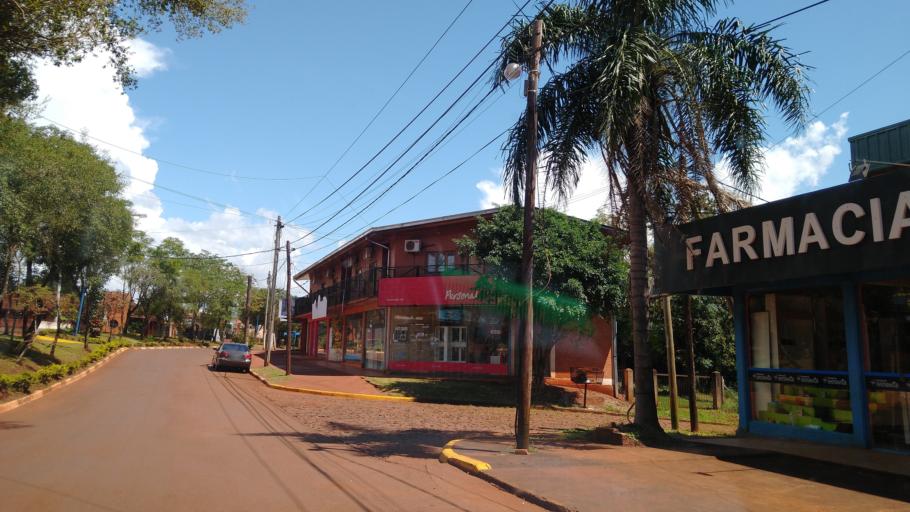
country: AR
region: Misiones
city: Puerto Libertad
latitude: -25.9721
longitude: -54.5632
